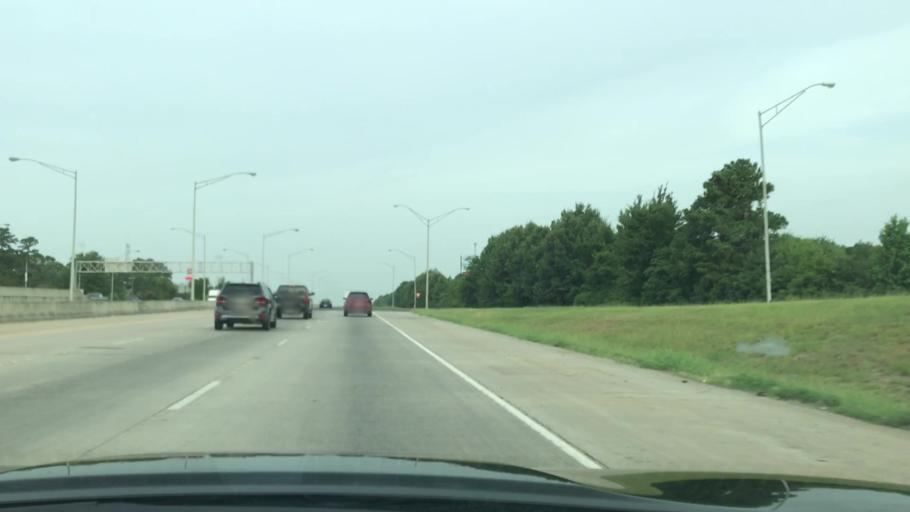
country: US
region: Louisiana
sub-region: Caddo Parish
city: Greenwood
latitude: 32.4505
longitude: -93.8683
